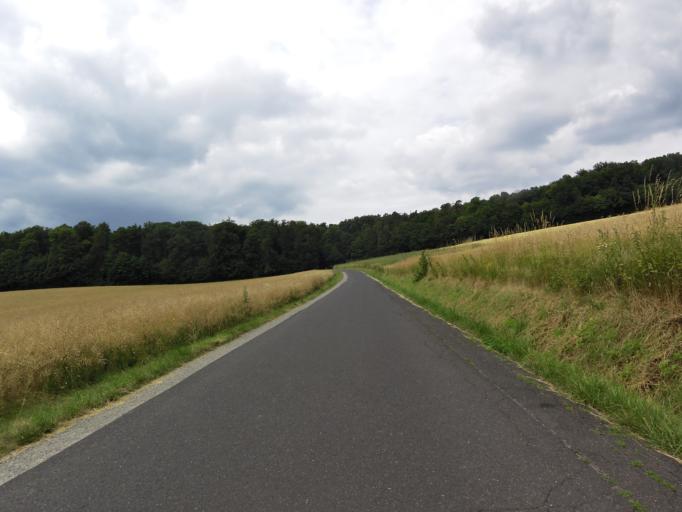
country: DE
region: Bavaria
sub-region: Regierungsbezirk Unterfranken
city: Reichenberg
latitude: 49.7581
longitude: 9.9192
